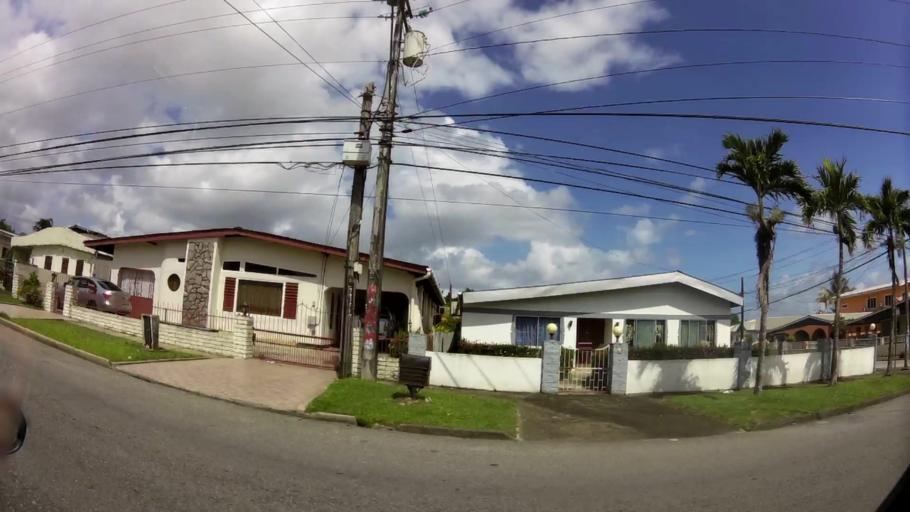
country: TT
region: Borough of Arima
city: Arima
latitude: 10.6223
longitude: -61.2643
